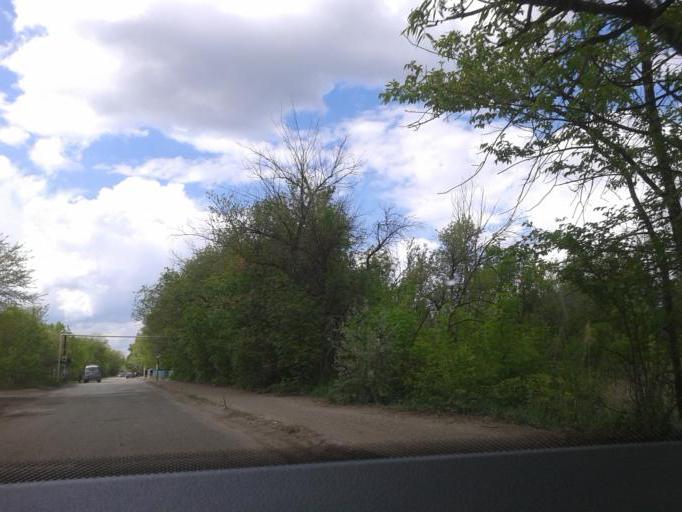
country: RU
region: Volgograd
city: Krasnoslobodsk
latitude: 48.5197
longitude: 44.5137
